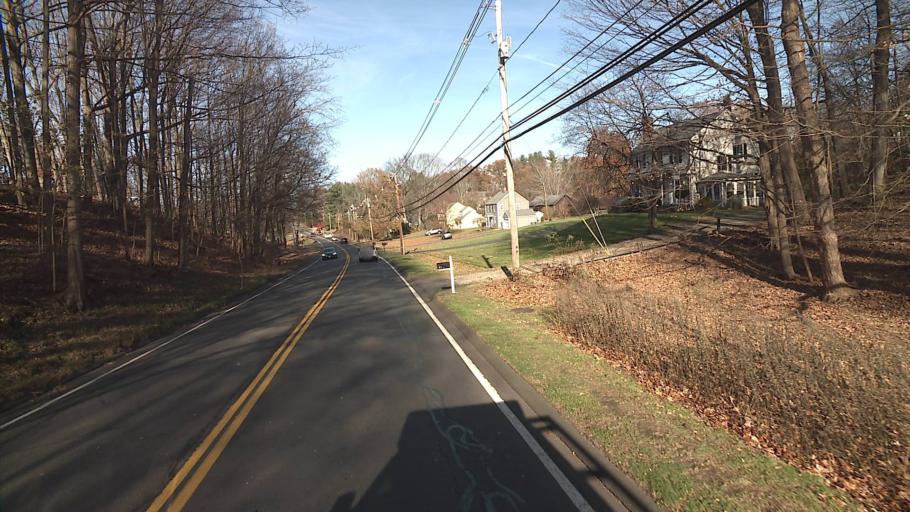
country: US
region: Connecticut
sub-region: Hartford County
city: Glastonbury Center
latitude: 41.6779
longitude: -72.5986
